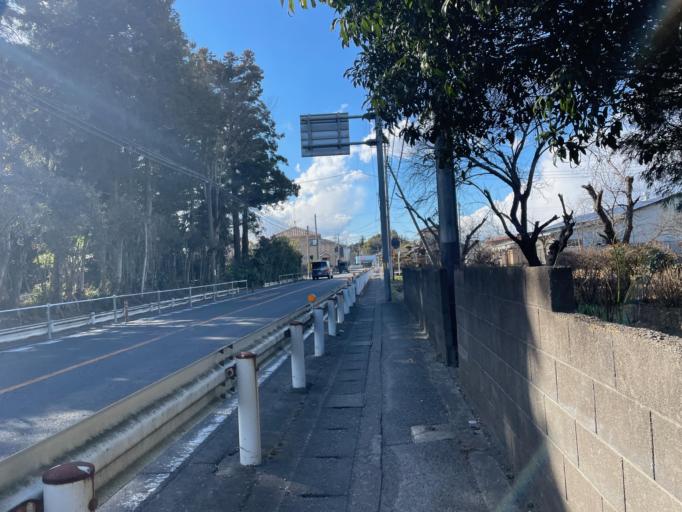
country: JP
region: Saitama
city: Ogawa
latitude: 36.0352
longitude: 139.3415
